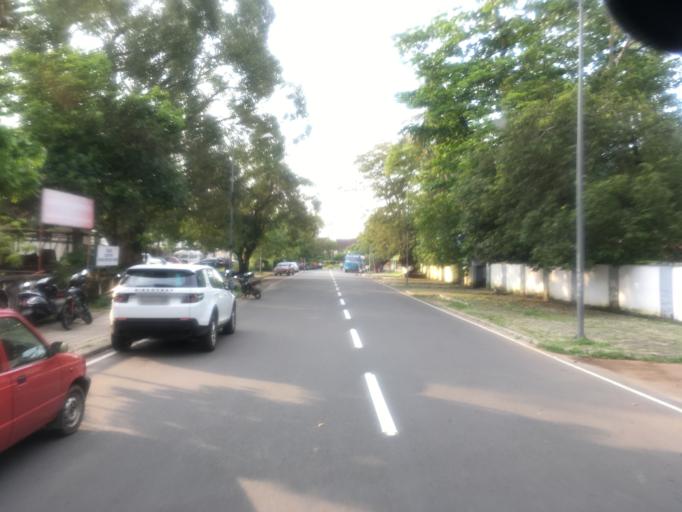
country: IN
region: Kerala
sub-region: Ernakulam
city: Cochin
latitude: 9.9684
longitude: 76.2605
